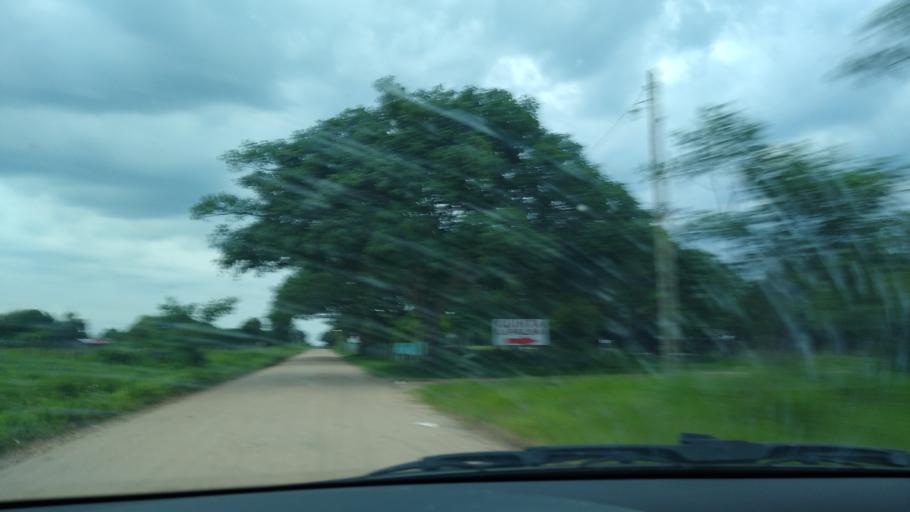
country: AR
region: Chaco
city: Puerto Vilelas
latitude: -27.5121
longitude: -58.9688
